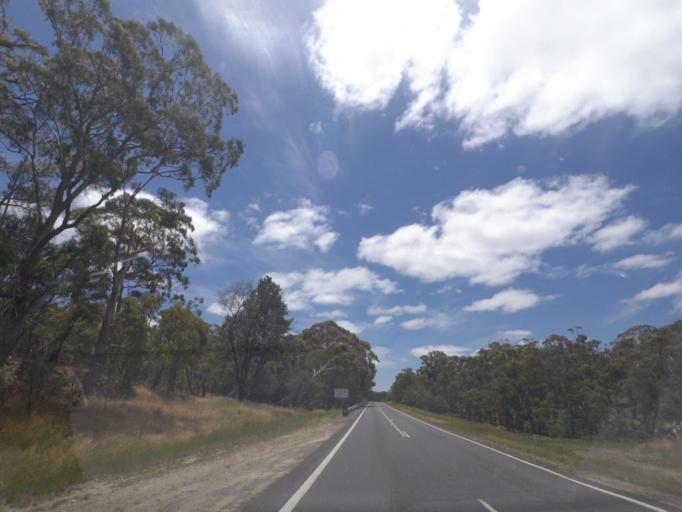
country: AU
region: Victoria
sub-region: Mount Alexander
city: Castlemaine
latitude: -37.2944
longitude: 144.1628
